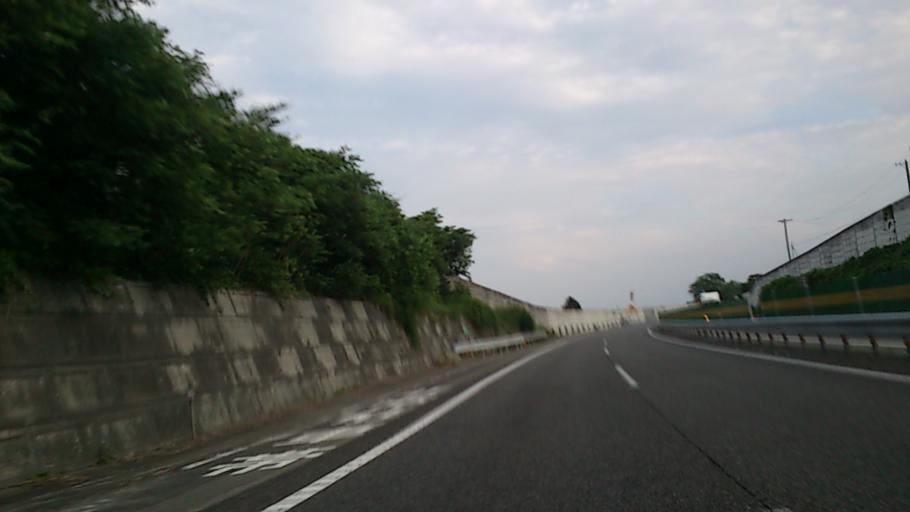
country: JP
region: Nagano
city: Ina
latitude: 35.7865
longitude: 137.9351
